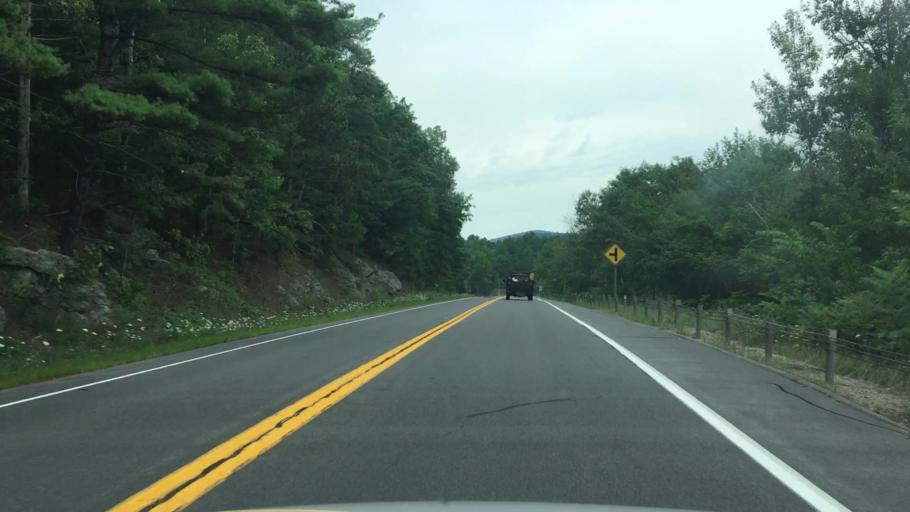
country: US
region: New York
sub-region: Essex County
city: Keeseville
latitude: 44.4588
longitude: -73.6270
